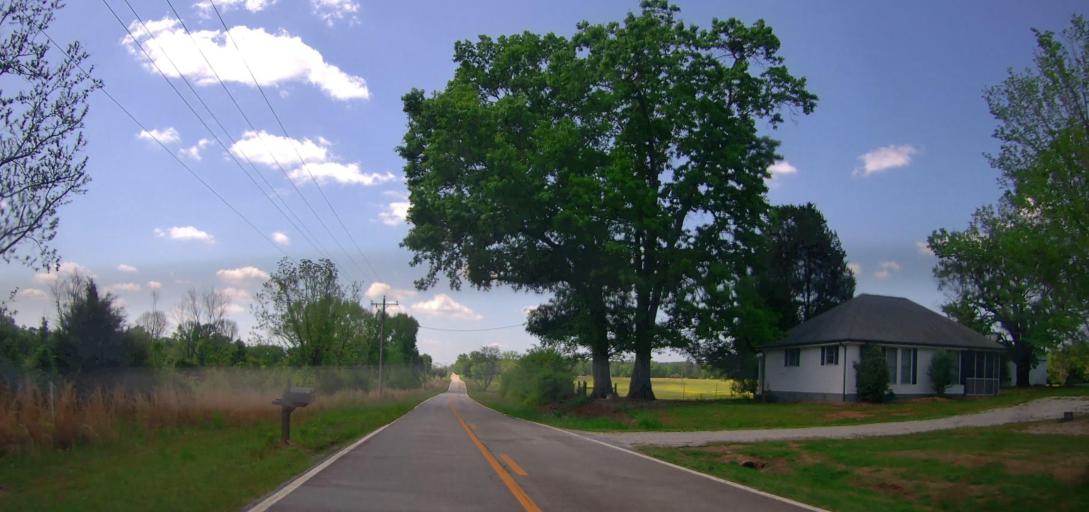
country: US
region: Georgia
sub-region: Putnam County
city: Eatonton
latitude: 33.3276
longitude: -83.3145
